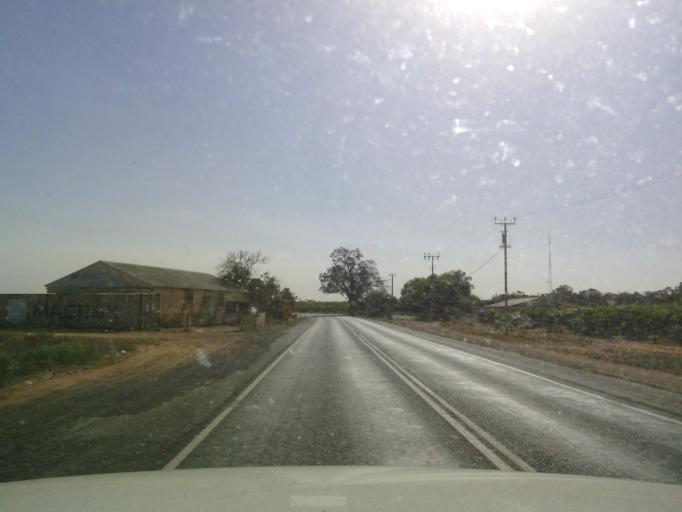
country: AU
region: South Australia
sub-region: Berri and Barmera
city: Berri
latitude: -34.2807
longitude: 140.5676
